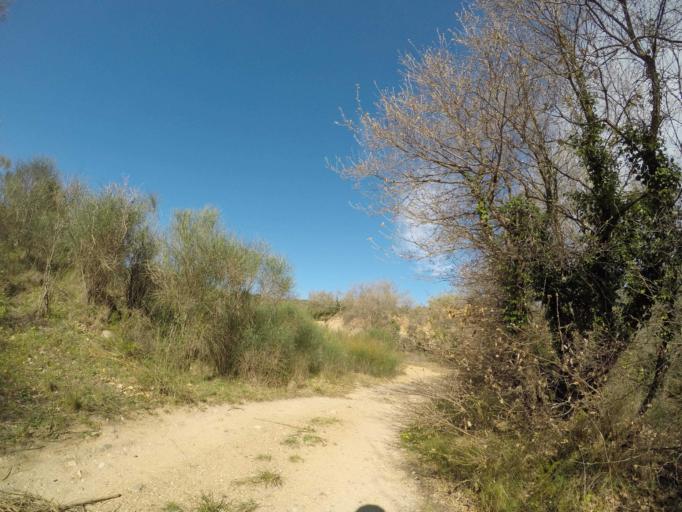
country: FR
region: Languedoc-Roussillon
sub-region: Departement des Pyrenees-Orientales
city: Millas
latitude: 42.7105
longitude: 2.6989
